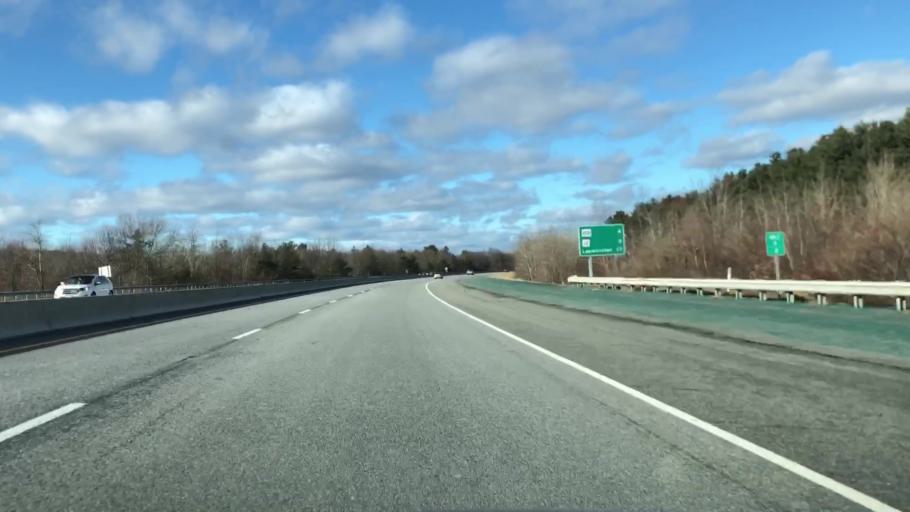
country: US
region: Massachusetts
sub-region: Worcester County
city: West Boylston
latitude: 42.3467
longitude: -71.8068
